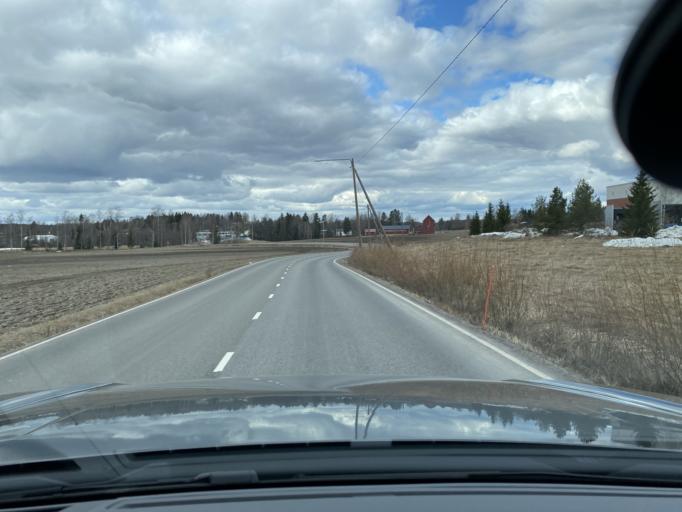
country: FI
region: Uusimaa
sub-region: Helsinki
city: Kilo
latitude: 60.3353
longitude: 24.8328
